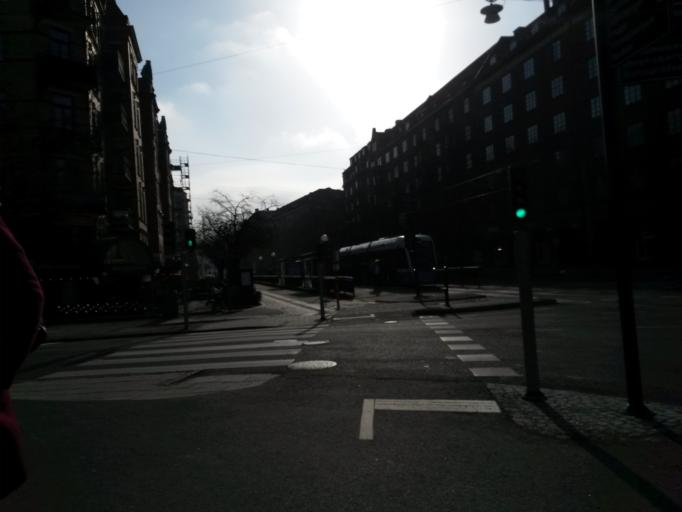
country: SE
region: Vaestra Goetaland
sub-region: Goteborg
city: Goeteborg
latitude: 57.6987
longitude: 11.9821
